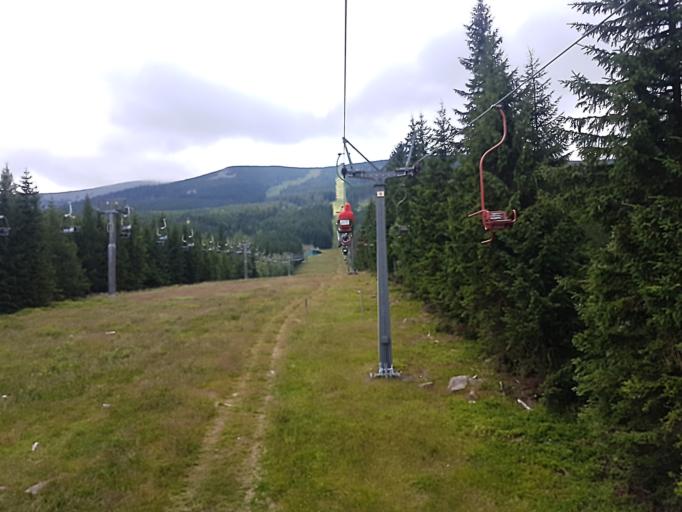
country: PL
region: Lower Silesian Voivodeship
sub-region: Powiat jeleniogorski
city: Karpacz
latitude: 50.7631
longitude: 15.7288
